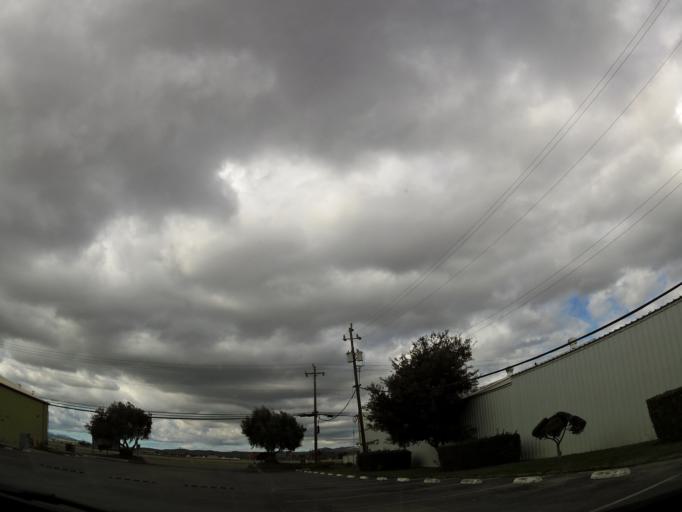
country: US
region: California
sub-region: San Benito County
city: Hollister
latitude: 36.8734
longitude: -121.4001
